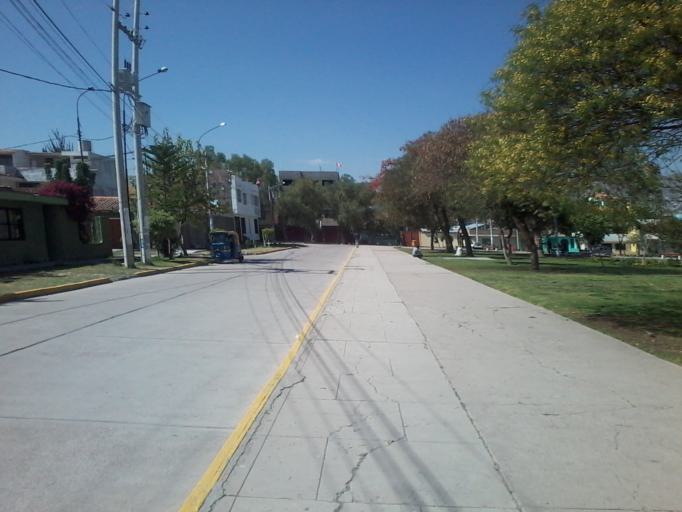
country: PE
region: Ayacucho
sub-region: Provincia de Huamanga
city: Ayacucho
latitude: -13.1619
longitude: -74.2131
